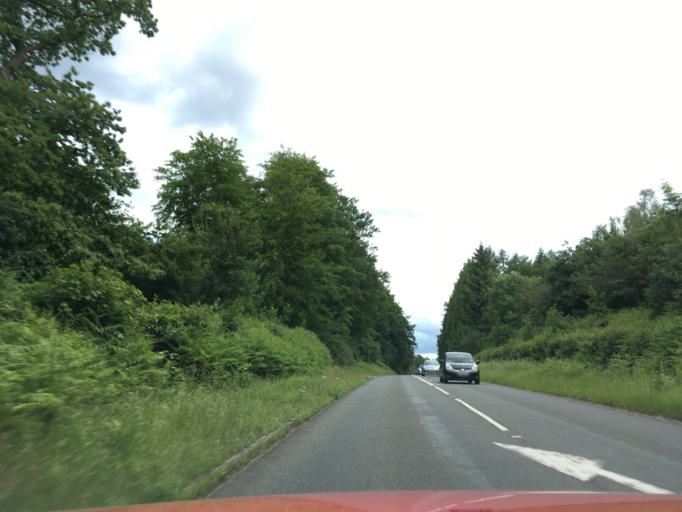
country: GB
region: England
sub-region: Oxfordshire
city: Boars Hill
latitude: 51.7194
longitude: -1.2672
